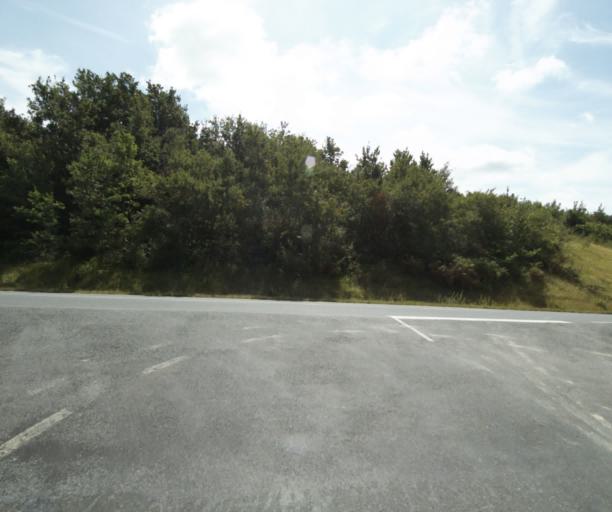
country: FR
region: Midi-Pyrenees
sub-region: Departement du Tarn
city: Dourgne
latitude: 43.4789
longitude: 2.1094
